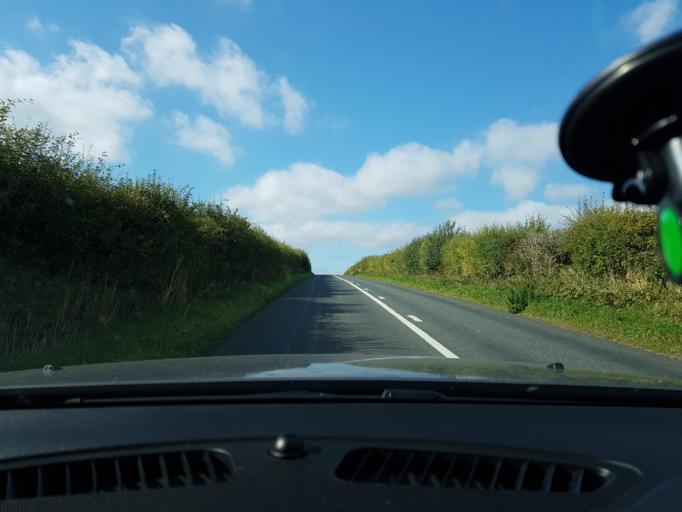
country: GB
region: England
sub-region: Wiltshire
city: Aldbourne
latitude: 51.4990
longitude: -1.6581
